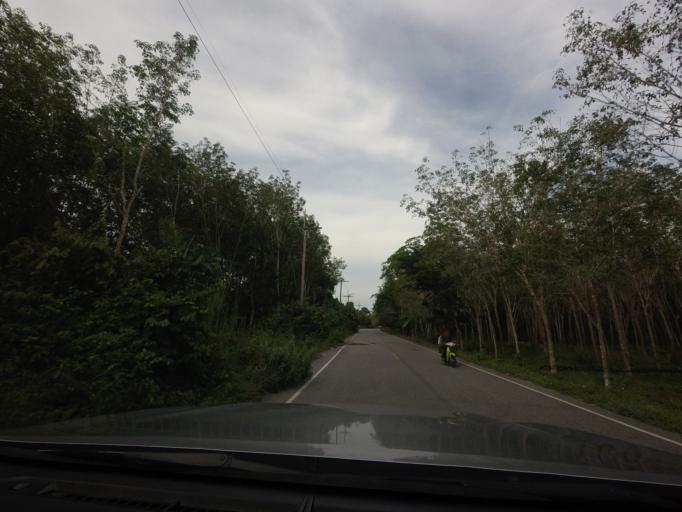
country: TH
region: Narathiwat
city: Rueso
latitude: 6.3530
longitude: 101.4692
